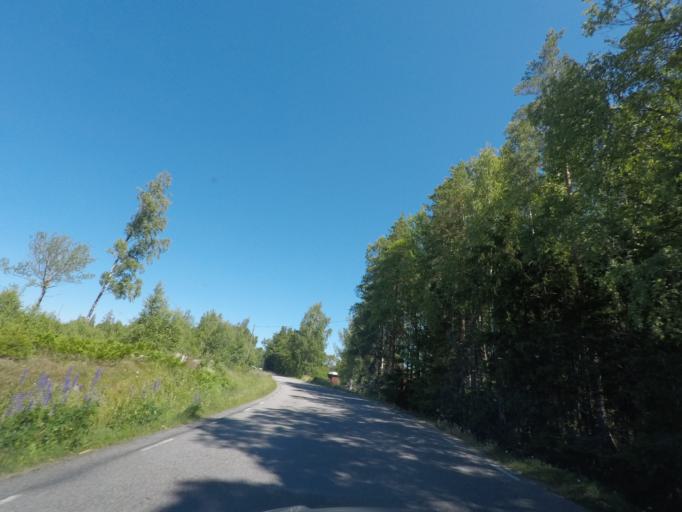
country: SE
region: Uppsala
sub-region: Enkopings Kommun
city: Irsta
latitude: 59.6728
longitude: 16.9025
